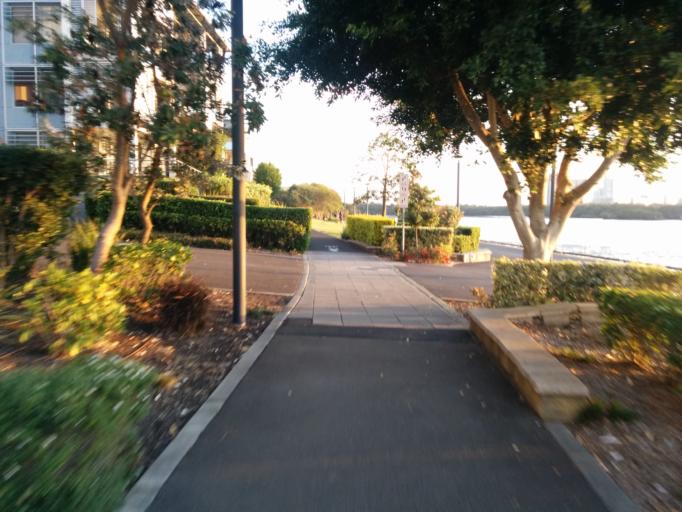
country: AU
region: New South Wales
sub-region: Canada Bay
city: Rhodes
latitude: -33.8331
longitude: 151.0832
